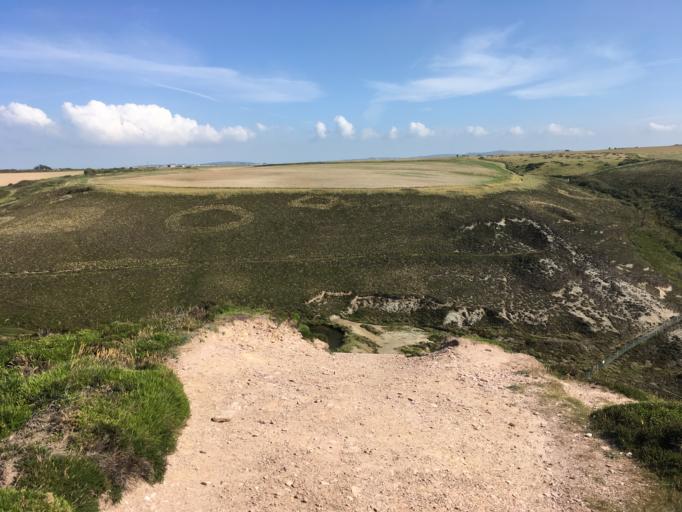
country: GB
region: England
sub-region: Cornwall
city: Redruth
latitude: 50.2778
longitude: -5.2593
